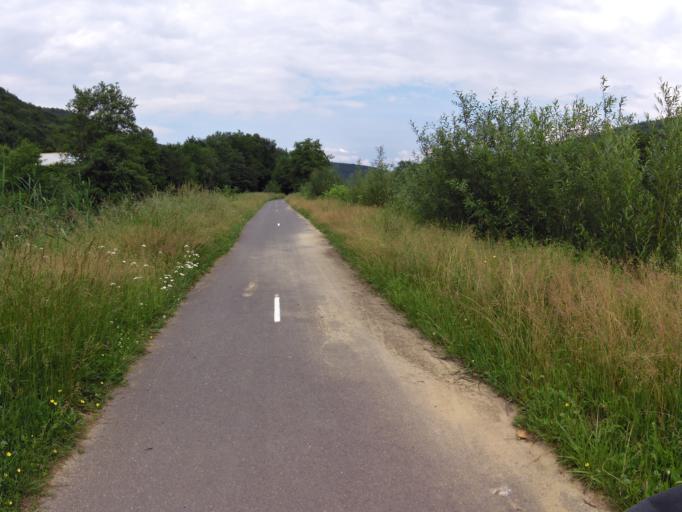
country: FR
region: Champagne-Ardenne
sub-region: Departement des Ardennes
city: Nouzonville
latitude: 49.8209
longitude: 4.7432
